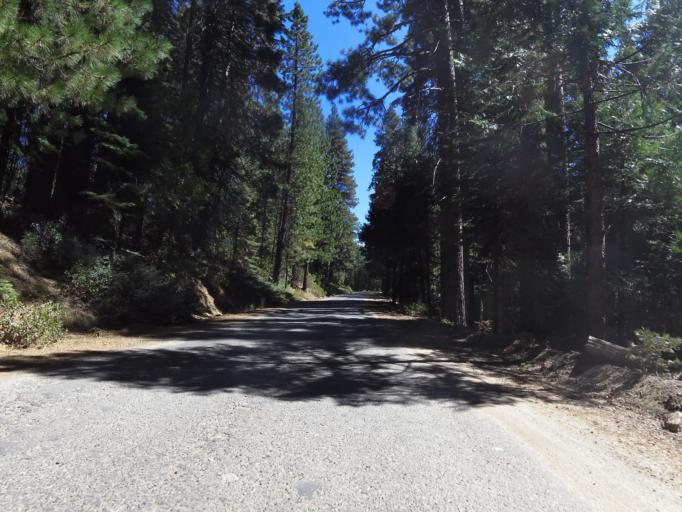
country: US
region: California
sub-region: Madera County
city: Oakhurst
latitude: 37.4364
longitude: -119.5433
